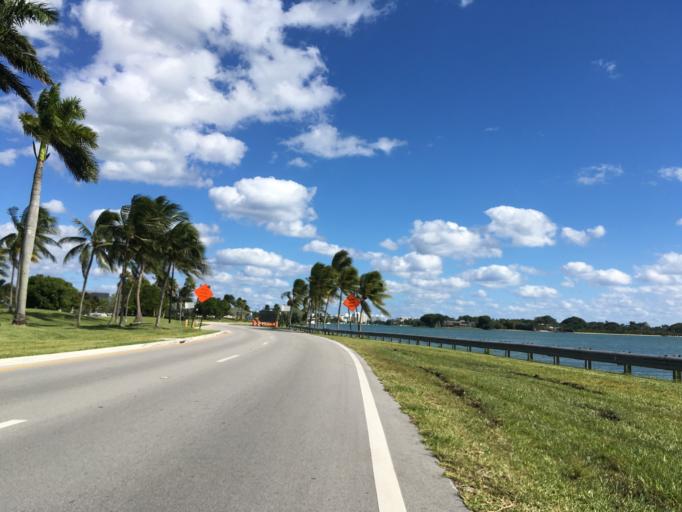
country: US
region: Florida
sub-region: Miami-Dade County
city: Bay Harbor Islands
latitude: 25.8884
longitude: -80.1481
